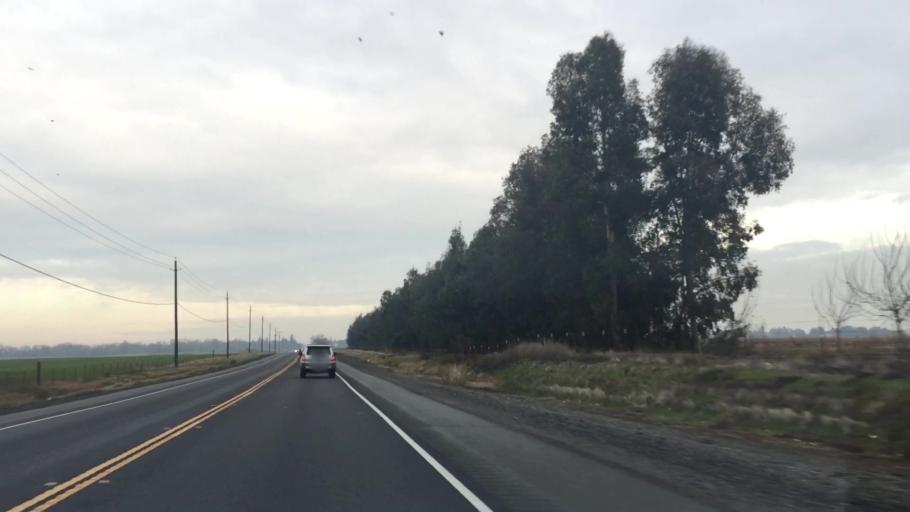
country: US
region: California
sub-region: Butte County
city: Palermo
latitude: 39.4097
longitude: -121.6048
